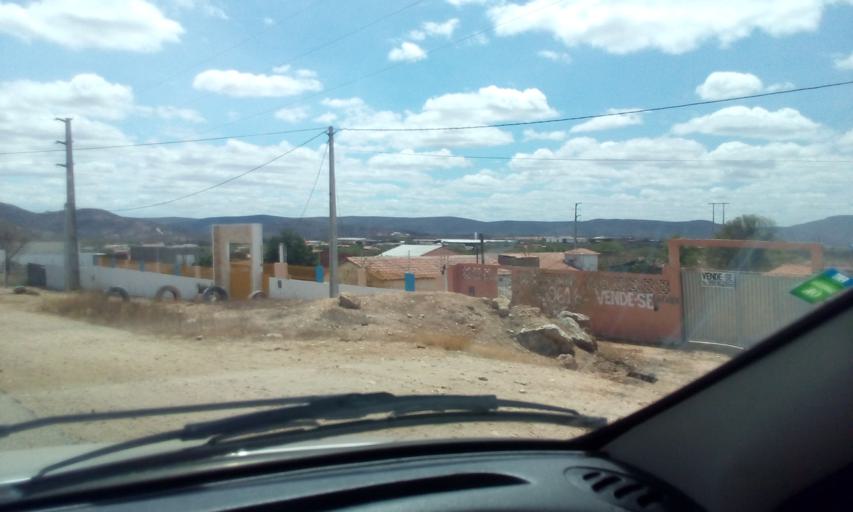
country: BR
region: Rio Grande do Norte
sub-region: Currais Novos
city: Currais Novos
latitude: -6.2779
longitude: -36.5288
